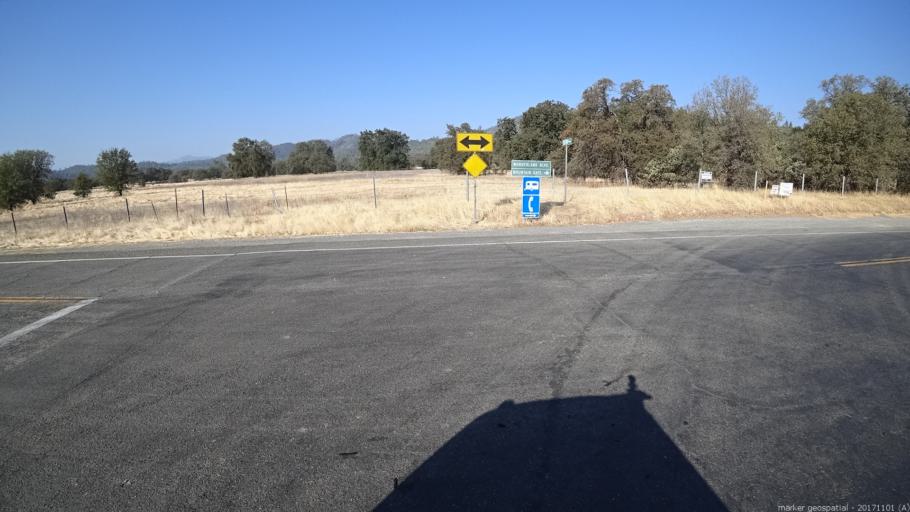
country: US
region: California
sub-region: Shasta County
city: Shasta Lake
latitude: 40.7065
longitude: -122.3390
